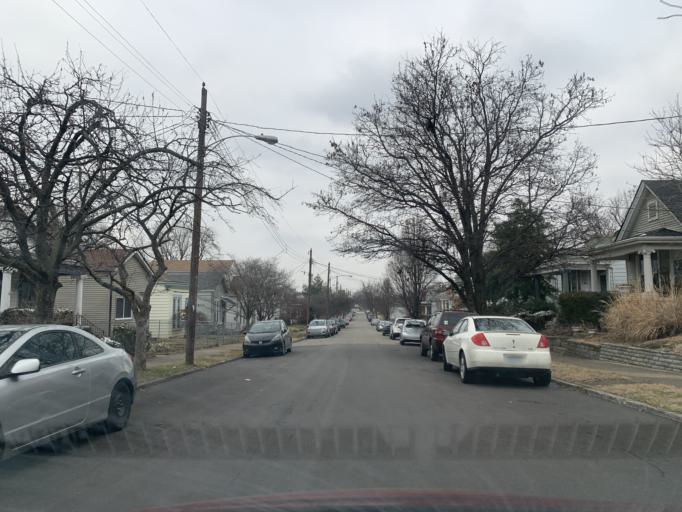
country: US
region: Kentucky
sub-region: Jefferson County
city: Audubon Park
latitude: 38.2249
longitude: -85.7383
